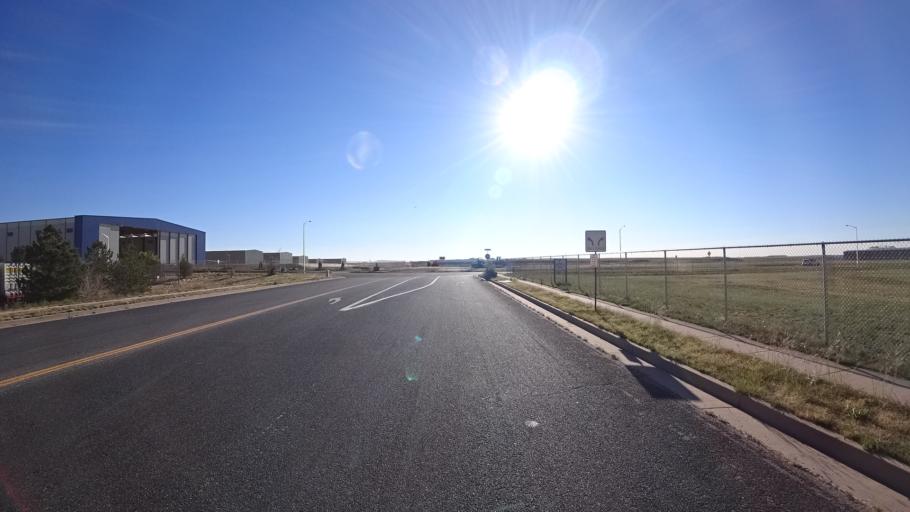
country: US
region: Colorado
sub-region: El Paso County
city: Security-Widefield
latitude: 38.7988
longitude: -104.7244
